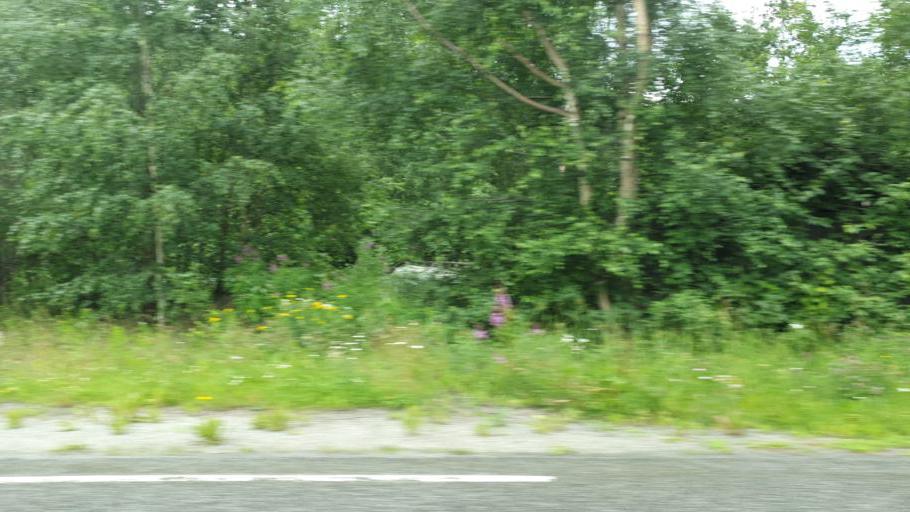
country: NO
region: Oppland
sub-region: Sel
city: Otta
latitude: 61.8419
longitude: 9.4071
